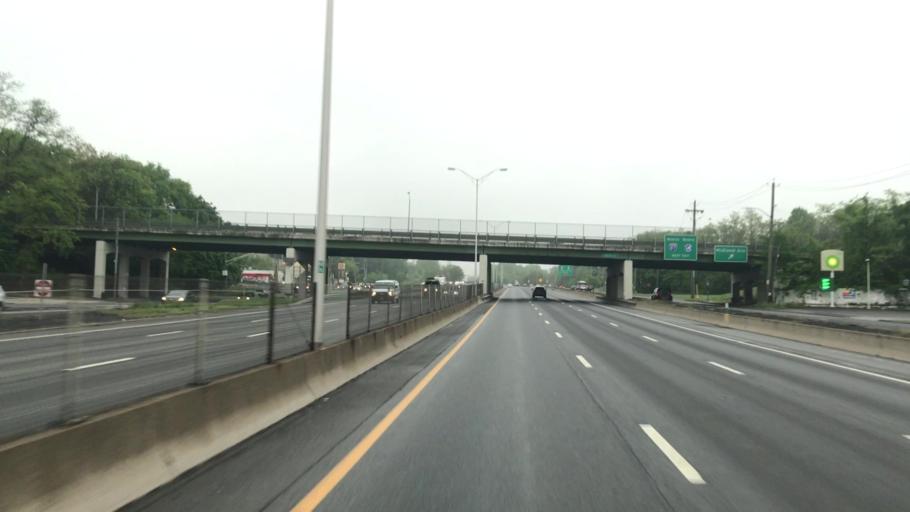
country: US
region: New York
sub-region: Westchester County
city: Bronxville
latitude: 40.9338
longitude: -73.8562
